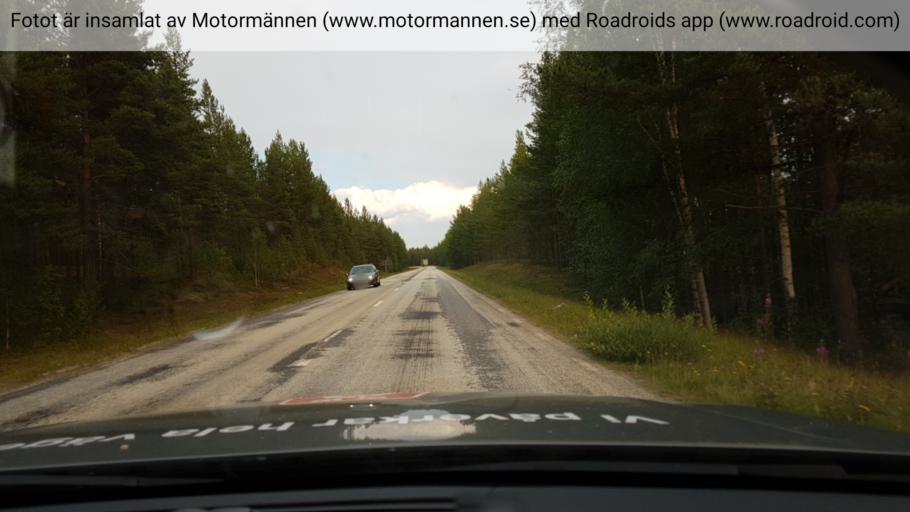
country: SE
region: Jaemtland
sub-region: Harjedalens Kommun
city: Sveg
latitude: 62.4069
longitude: 13.7006
